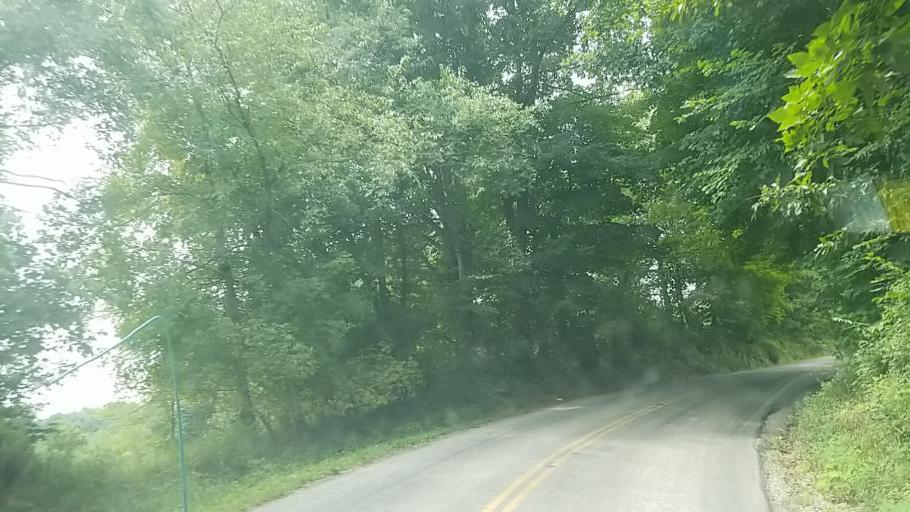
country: US
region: Ohio
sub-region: Licking County
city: Utica
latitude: 40.2313
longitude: -82.3365
